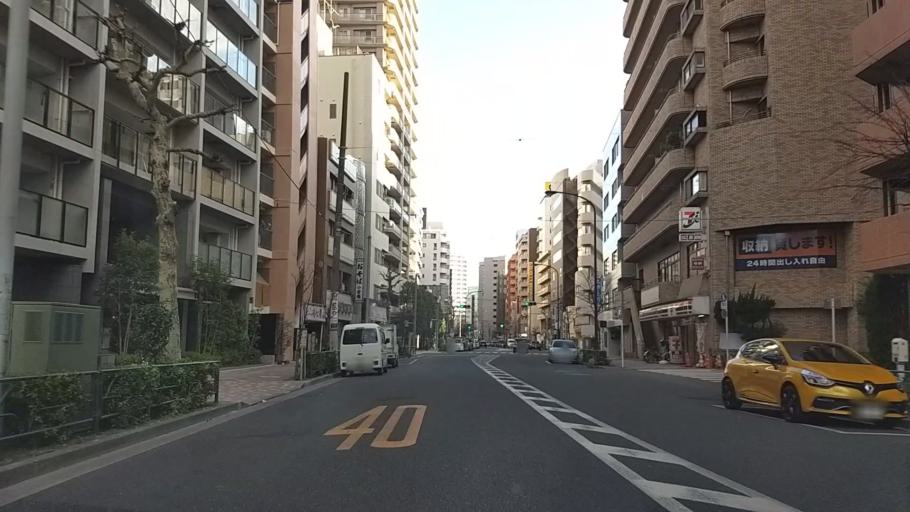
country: JP
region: Tokyo
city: Tokyo
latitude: 35.7349
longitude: 139.7272
